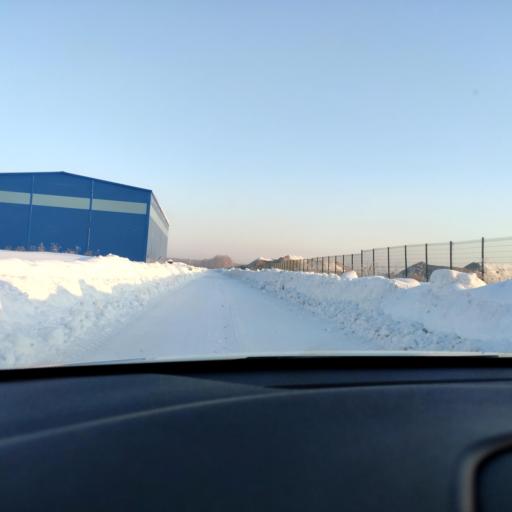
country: RU
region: Tatarstan
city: Staroye Arakchino
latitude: 55.8885
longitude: 48.9702
